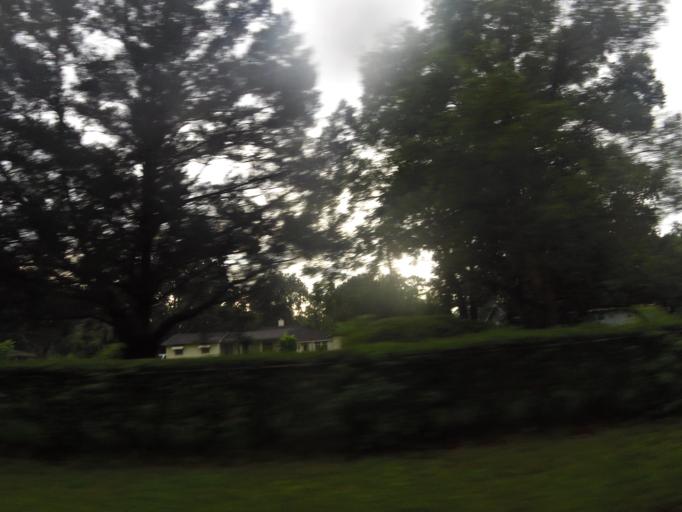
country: US
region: Florida
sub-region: Duval County
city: Jacksonville
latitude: 30.2652
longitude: -81.5773
